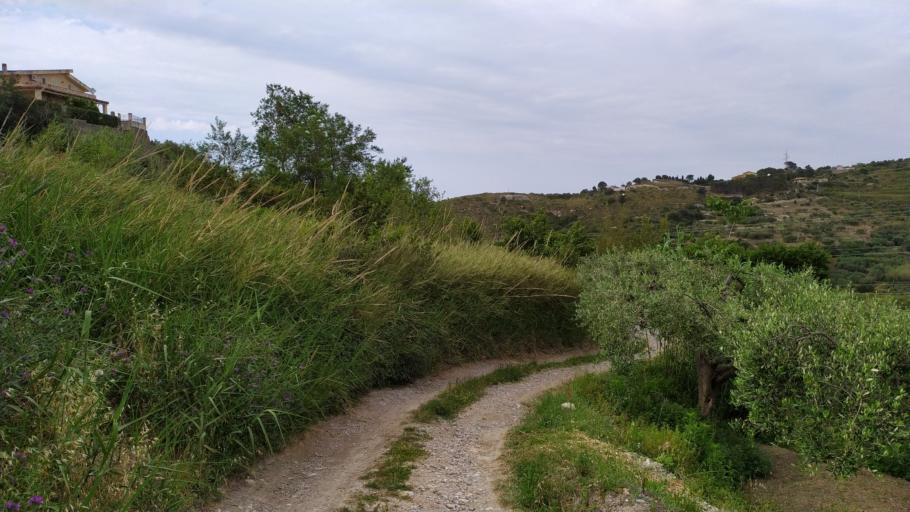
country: IT
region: Sicily
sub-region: Messina
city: Pace del Mela
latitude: 38.1613
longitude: 15.2945
